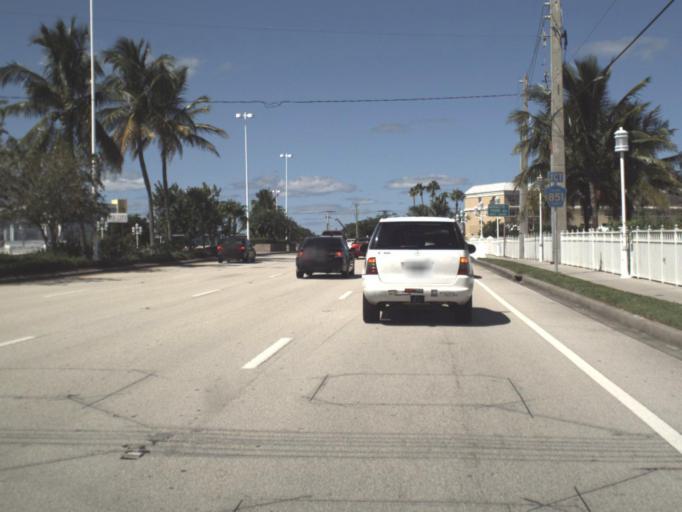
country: US
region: Florida
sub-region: Collier County
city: Naples
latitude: 26.1415
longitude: -81.7886
